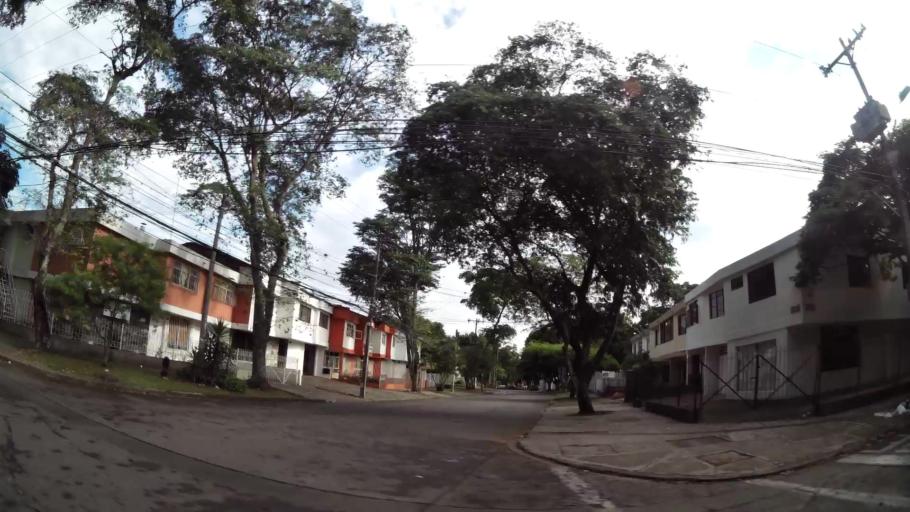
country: CO
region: Valle del Cauca
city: Cali
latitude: 3.4827
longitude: -76.5238
